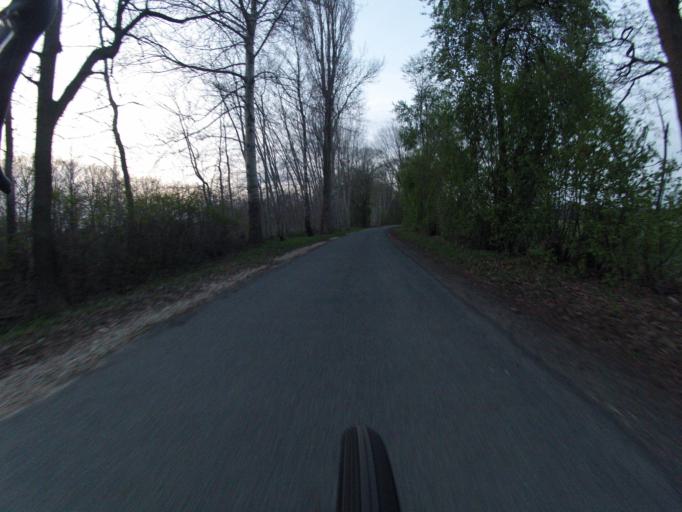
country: DE
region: North Rhine-Westphalia
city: Ibbenburen
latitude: 52.2514
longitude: 7.7531
